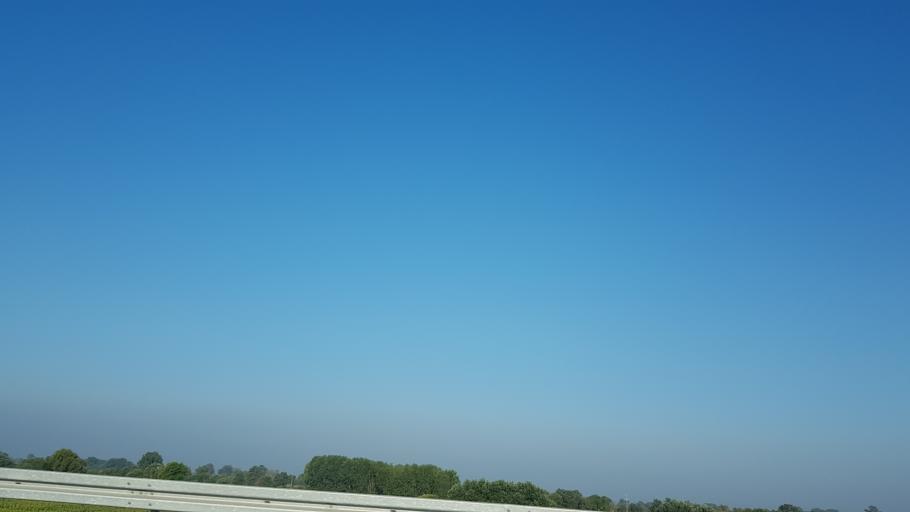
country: TR
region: Bursa
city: Tatkavakli
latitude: 40.1111
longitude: 28.2770
